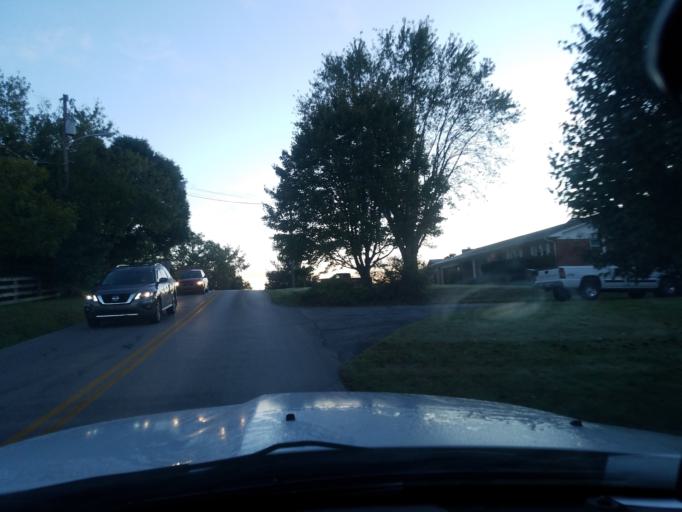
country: US
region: Kentucky
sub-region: Laurel County
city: London
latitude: 37.0957
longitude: -84.0793
